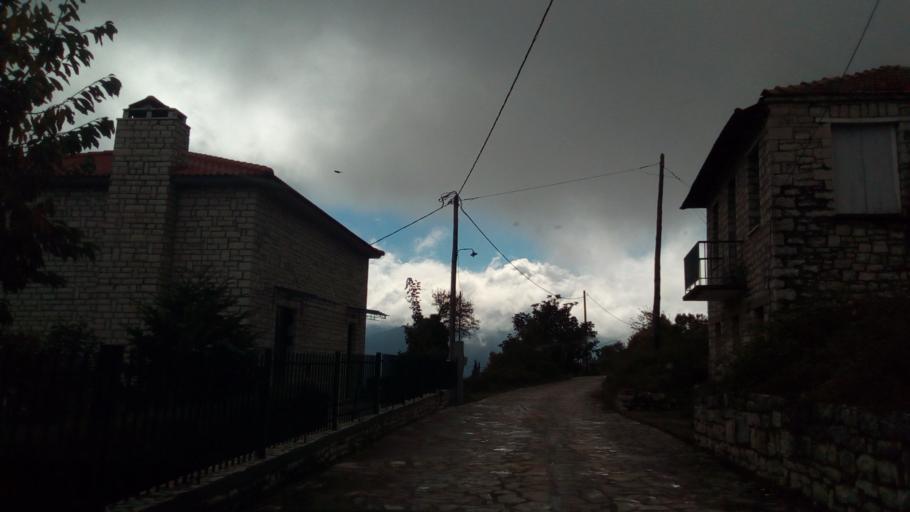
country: GR
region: West Greece
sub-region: Nomos Aitolias kai Akarnanias
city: Thermo
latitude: 38.5966
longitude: 21.7933
